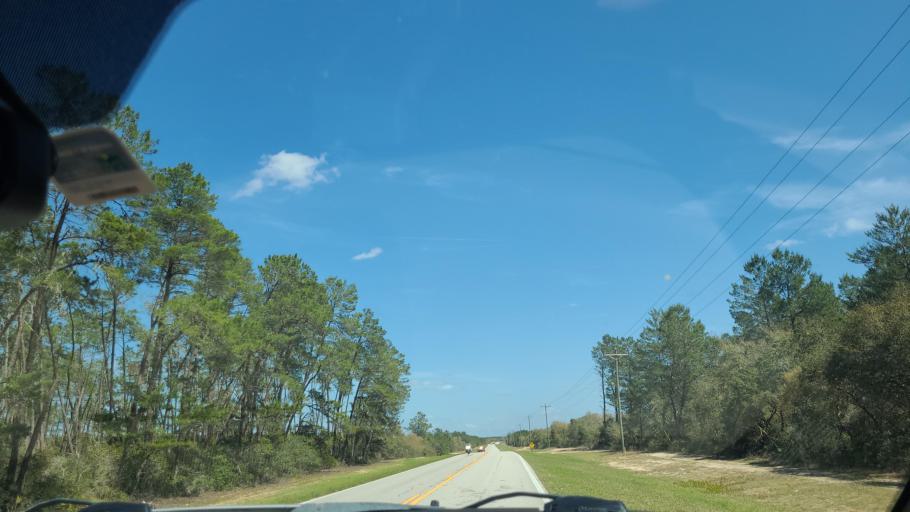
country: US
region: Florida
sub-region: Putnam County
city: Interlachen
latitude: 29.3681
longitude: -81.8536
